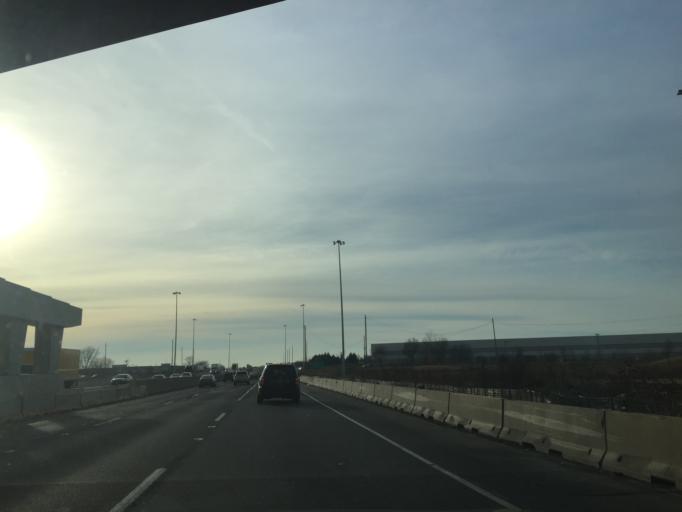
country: US
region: Illinois
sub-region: Will County
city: Romeoville
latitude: 41.6556
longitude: -88.1250
